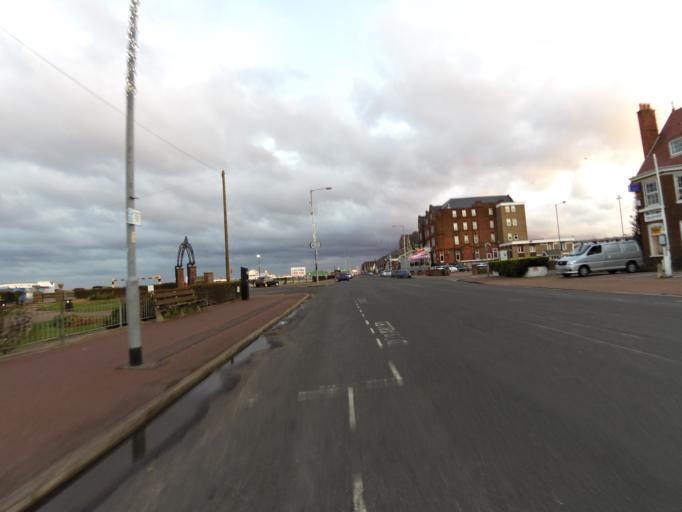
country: GB
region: England
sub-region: Norfolk
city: Great Yarmouth
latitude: 52.6138
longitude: 1.7380
